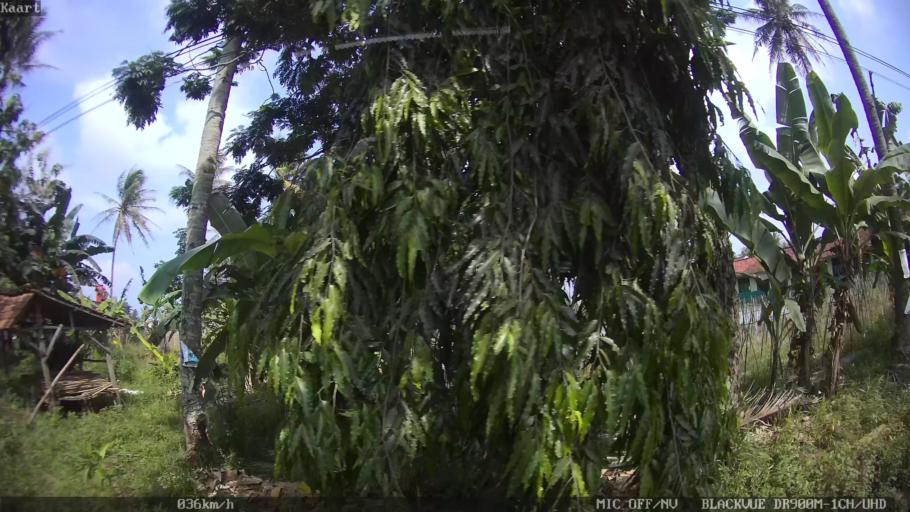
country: ID
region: Lampung
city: Kedaton
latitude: -5.3244
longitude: 105.2849
